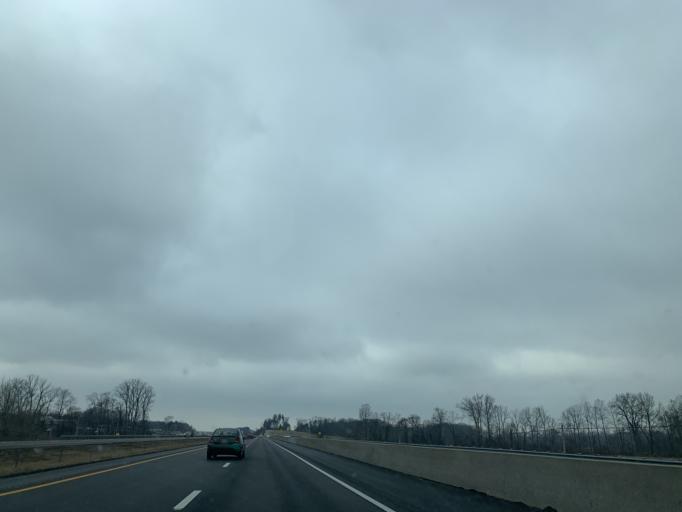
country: US
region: Ohio
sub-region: Licking County
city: Granville South
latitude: 40.0692
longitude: -82.5570
